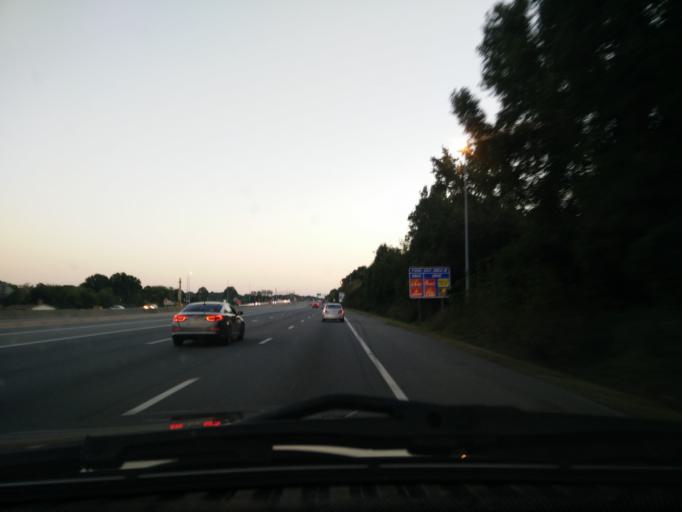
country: US
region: Virginia
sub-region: City of Chesapeake
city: Chesapeake
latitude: 36.8360
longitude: -76.1965
